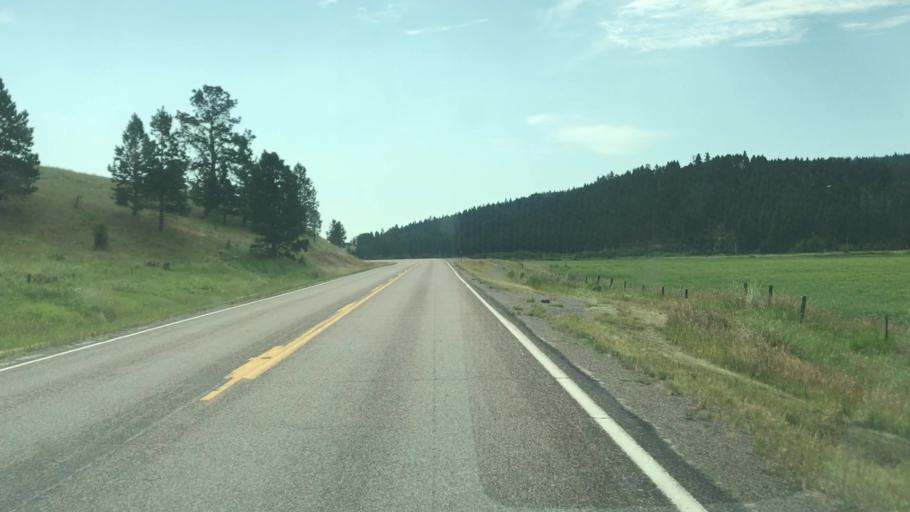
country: US
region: Montana
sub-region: Lewis and Clark County
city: Lincoln
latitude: 46.8073
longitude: -112.8236
